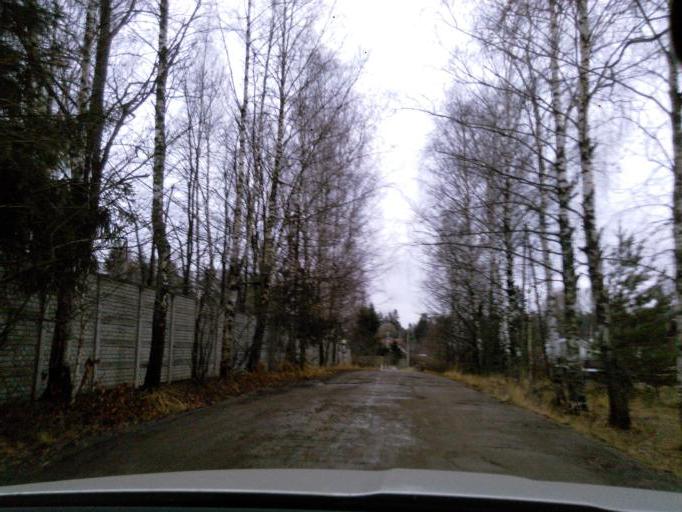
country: RU
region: Moskovskaya
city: Lozhki
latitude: 56.0550
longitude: 37.0981
